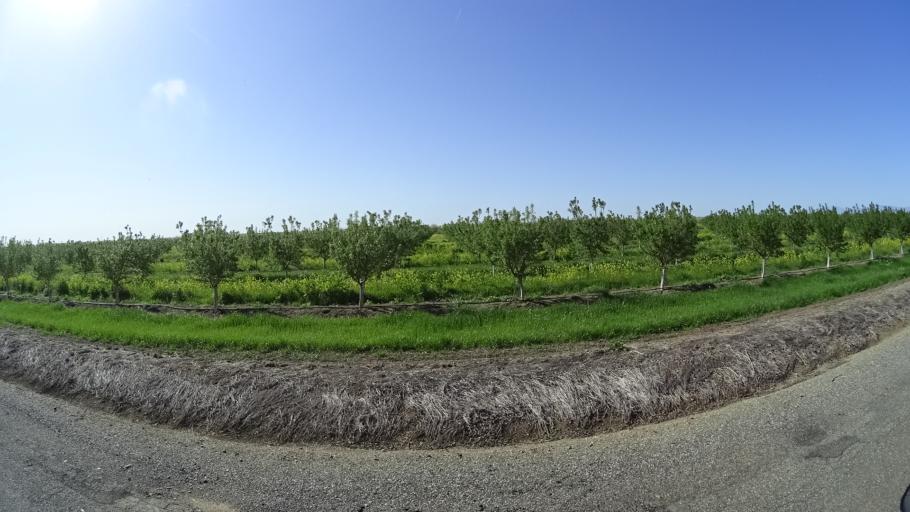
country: US
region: California
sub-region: Glenn County
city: Hamilton City
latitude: 39.7757
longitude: -122.0901
